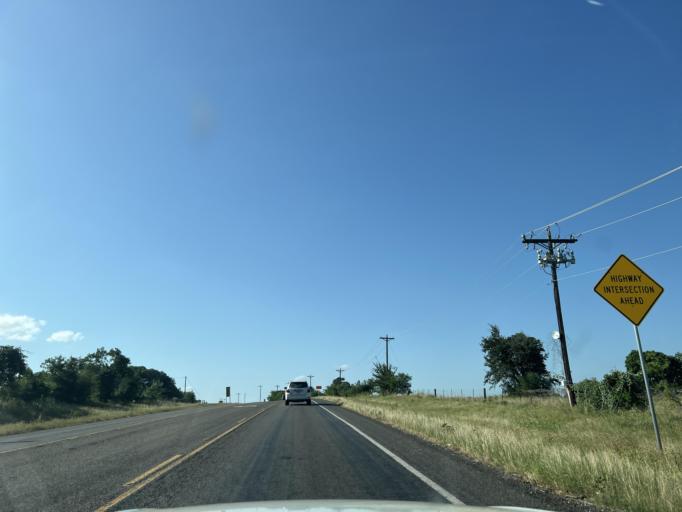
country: US
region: Texas
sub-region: Washington County
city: Brenham
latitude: 30.1728
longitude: -96.3816
